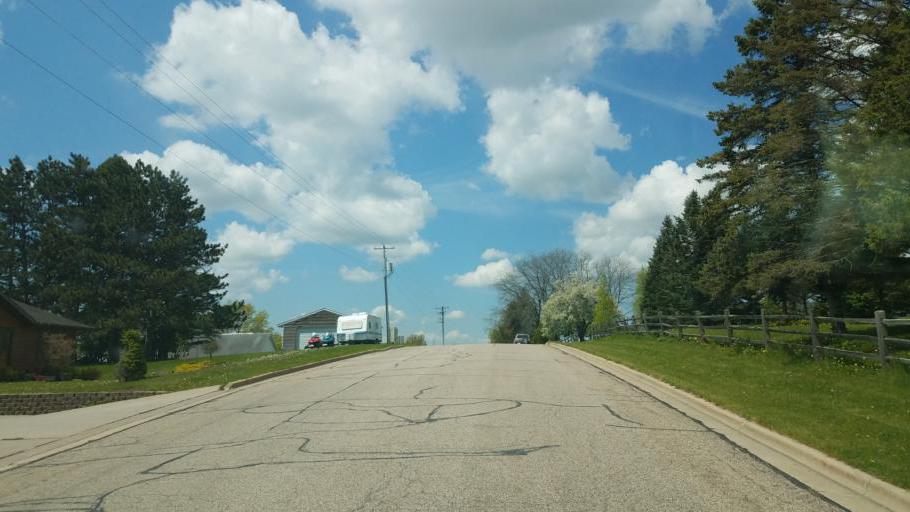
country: US
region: Wisconsin
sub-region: Vernon County
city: Hillsboro
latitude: 43.6585
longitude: -90.3473
